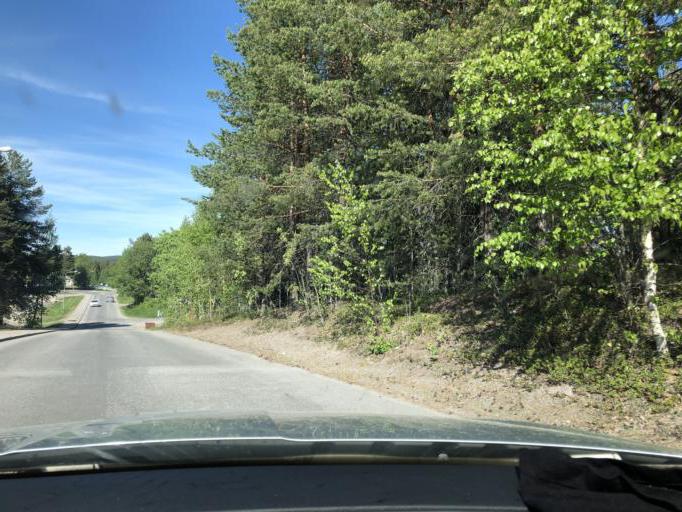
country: SE
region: Norrbotten
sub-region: Jokkmokks Kommun
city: Jokkmokk
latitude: 66.6018
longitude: 19.8461
